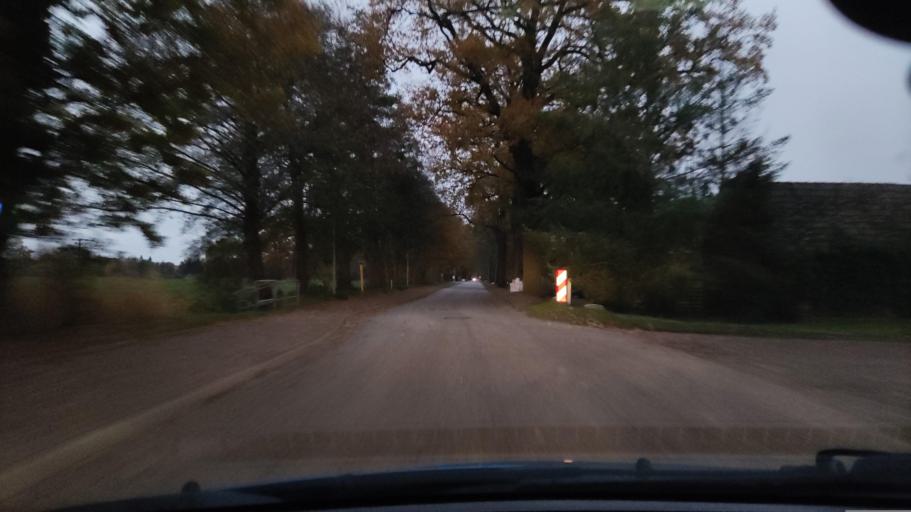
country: DE
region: Mecklenburg-Vorpommern
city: Neu Kaliss
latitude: 53.1799
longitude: 11.2797
